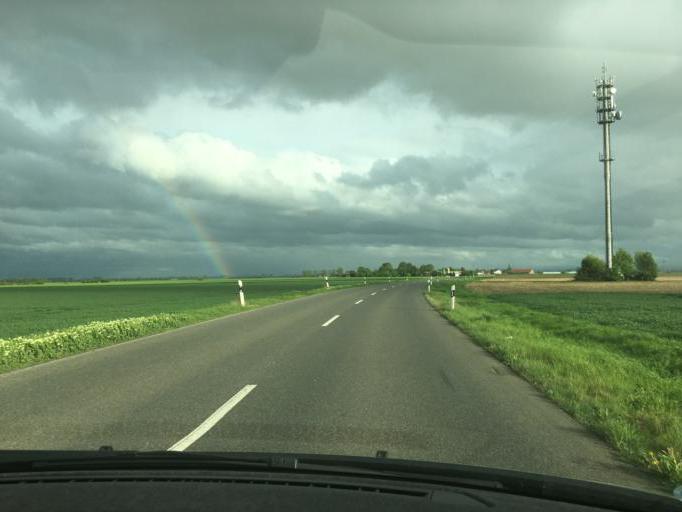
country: DE
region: North Rhine-Westphalia
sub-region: Regierungsbezirk Koln
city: Merzenich
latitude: 50.8086
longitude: 6.5583
